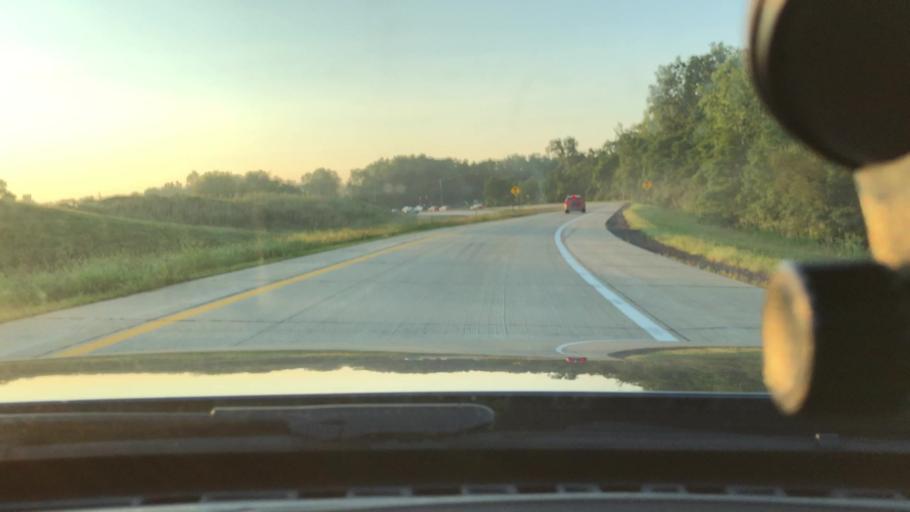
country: US
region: Michigan
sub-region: Wayne County
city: Plymouth
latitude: 42.3815
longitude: -83.5139
